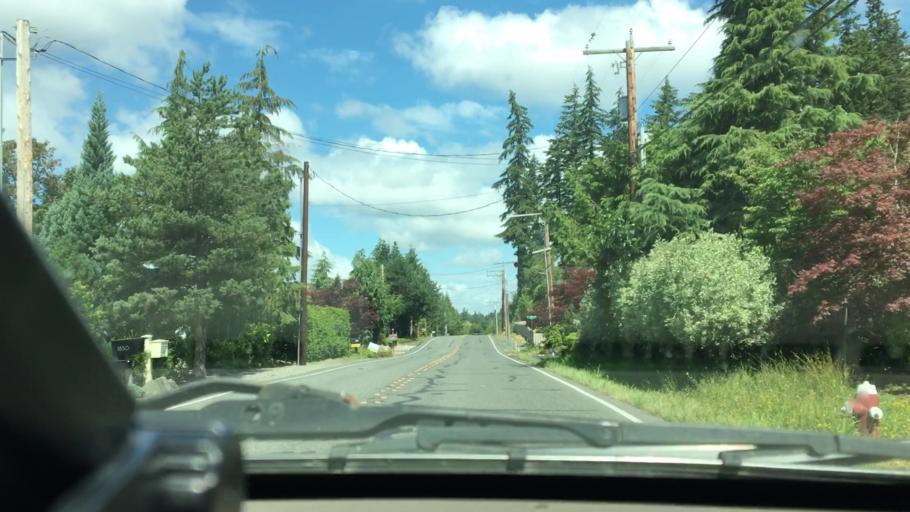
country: US
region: Washington
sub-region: Whatcom County
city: Geneva
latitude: 48.7611
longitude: -122.4010
